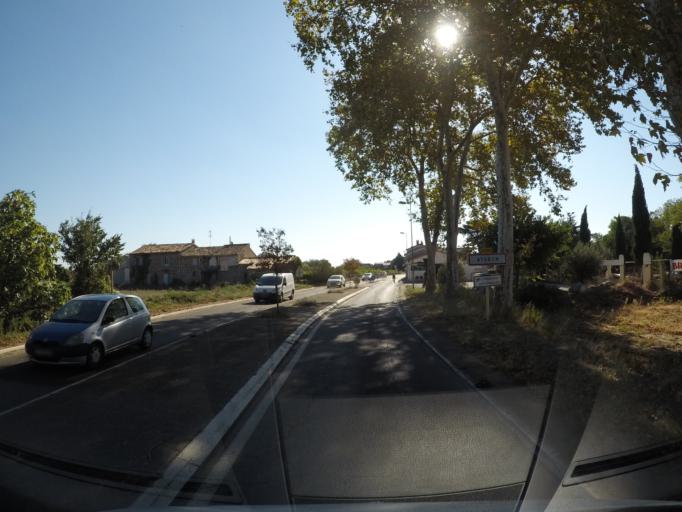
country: FR
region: Languedoc-Roussillon
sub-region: Departement du Gard
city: Boisset-et-Gaujac
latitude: 44.0294
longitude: 4.0160
